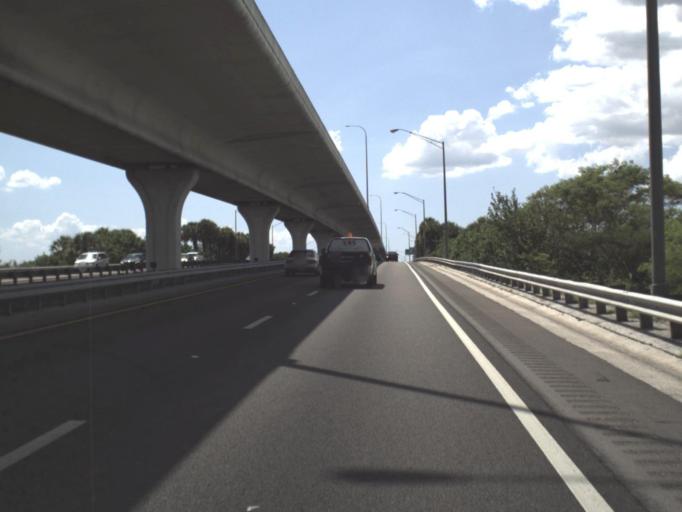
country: US
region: Florida
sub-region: Hillsborough County
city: Palm River-Clair Mel
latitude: 27.9501
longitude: -82.3941
